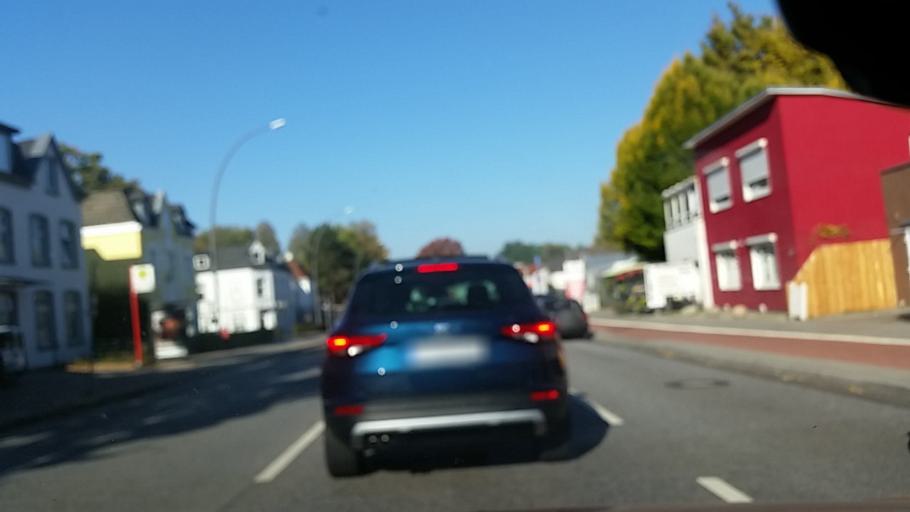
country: DE
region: Hamburg
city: Eidelstedt
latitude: 53.5836
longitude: 9.8812
